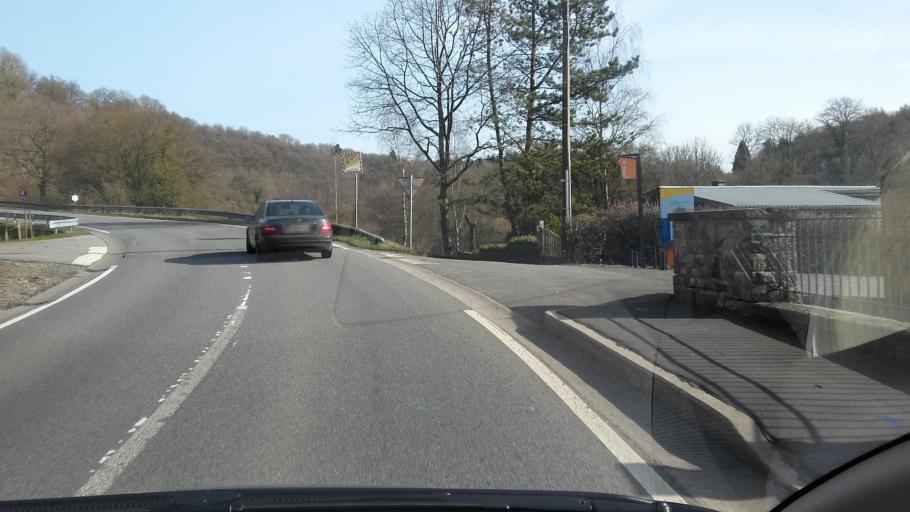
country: BE
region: Wallonia
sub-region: Province de Liege
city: Hamoir
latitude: 50.3956
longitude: 5.5516
